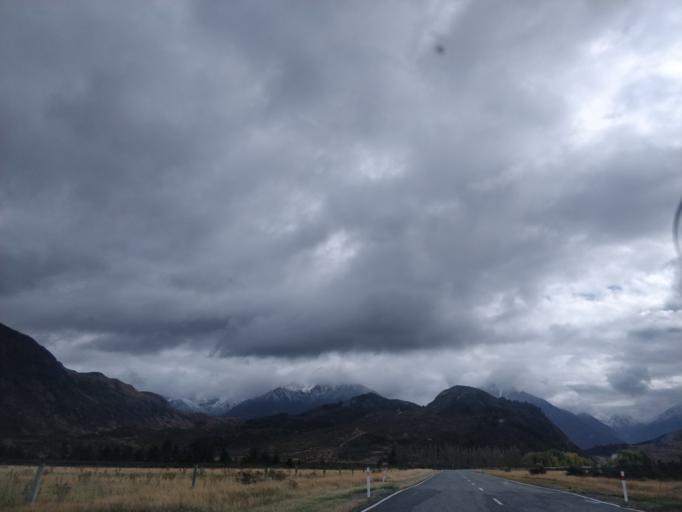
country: NZ
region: Canterbury
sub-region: Waimakariri District
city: Oxford
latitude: -43.0342
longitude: 171.7486
